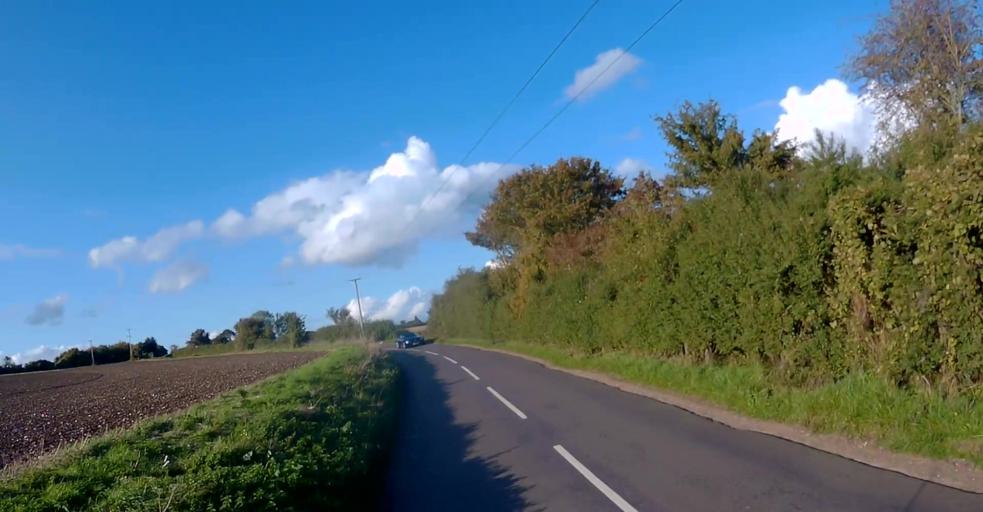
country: GB
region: England
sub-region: Hampshire
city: Odiham
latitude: 51.2457
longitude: -0.9337
